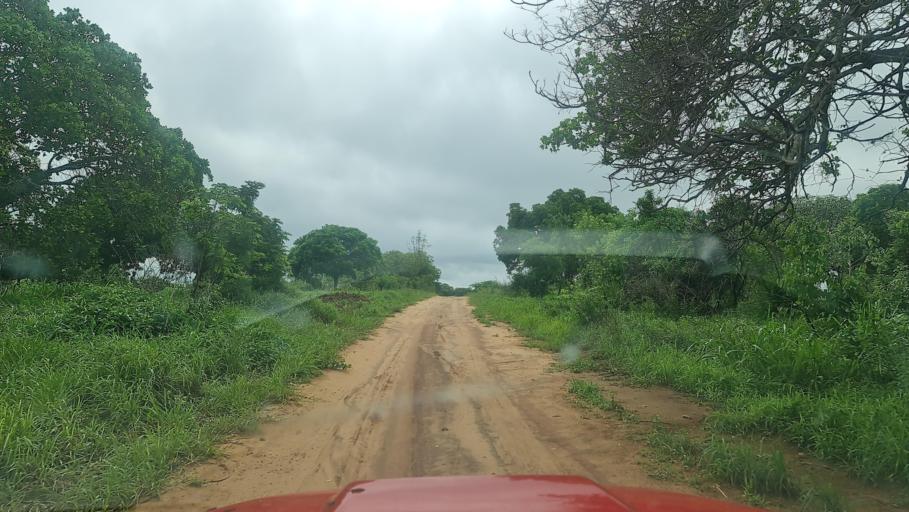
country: MW
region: Southern Region
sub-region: Nsanje District
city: Nsanje
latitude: -17.1926
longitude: 35.8532
